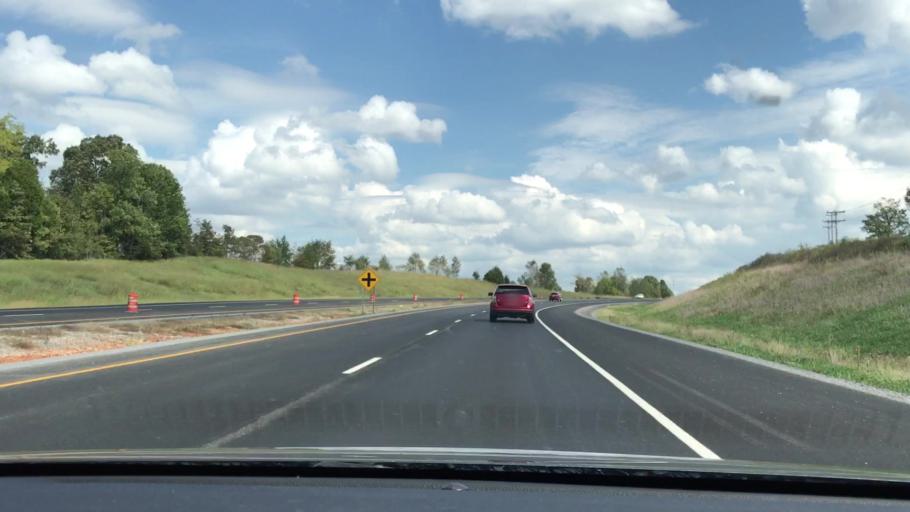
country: US
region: Kentucky
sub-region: Trigg County
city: Cadiz
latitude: 36.8575
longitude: -87.8132
